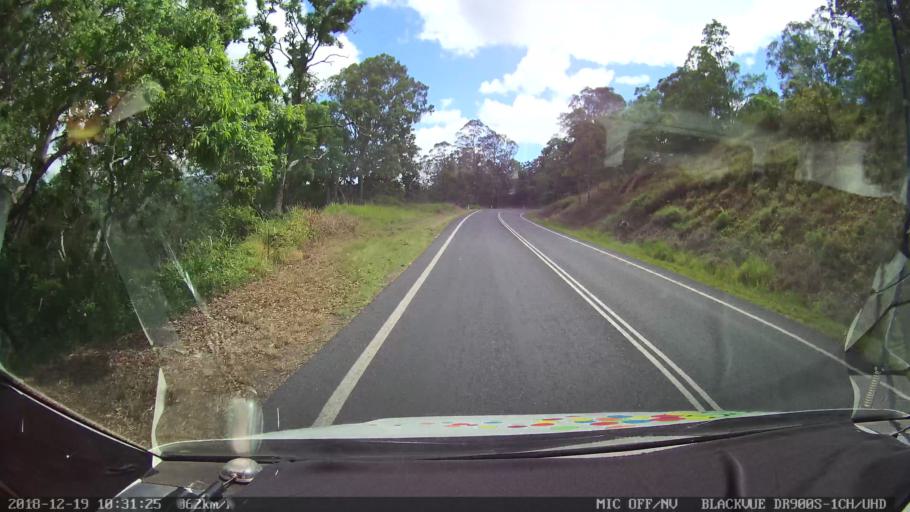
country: AU
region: New South Wales
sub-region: Lismore Municipality
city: Larnook
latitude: -28.5894
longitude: 153.1161
